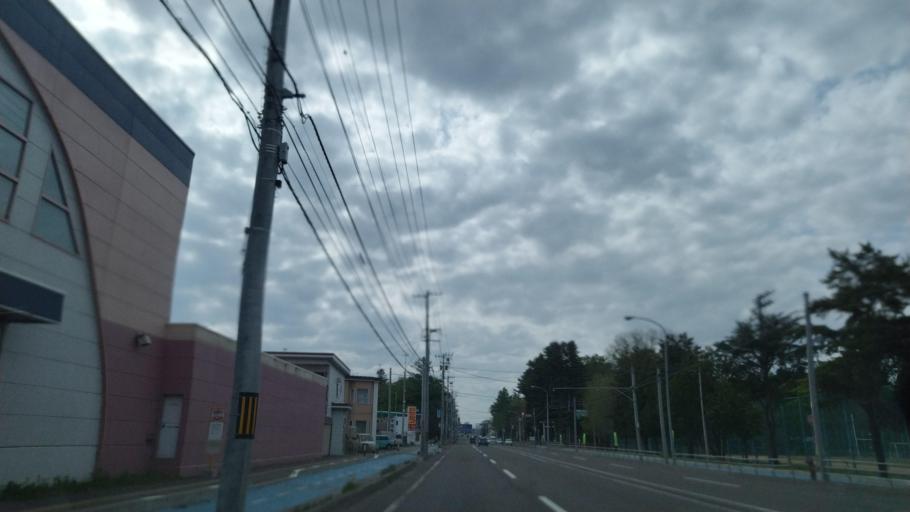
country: JP
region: Hokkaido
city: Obihiro
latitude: 42.9295
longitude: 143.2125
